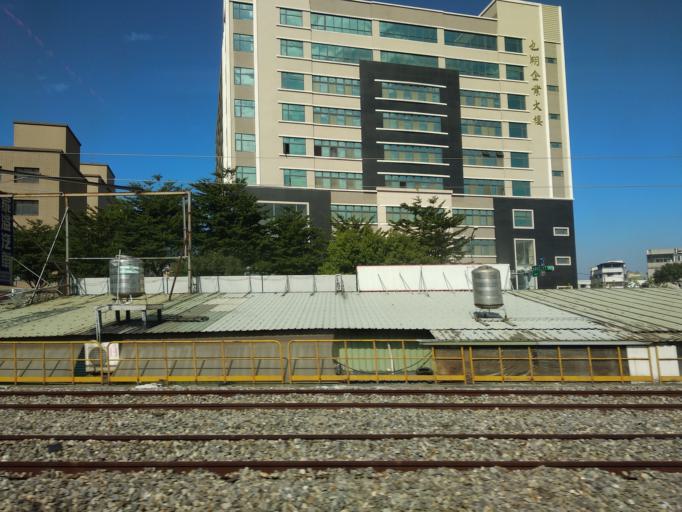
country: TW
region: Taiwan
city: Taoyuan City
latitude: 24.9800
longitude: 121.2746
